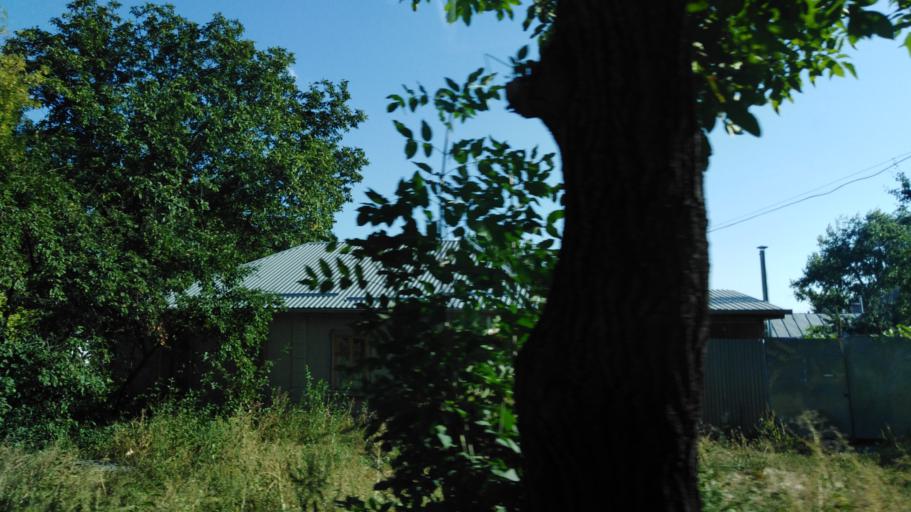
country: RU
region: Stavropol'skiy
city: Svobody
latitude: 44.0384
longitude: 43.0439
